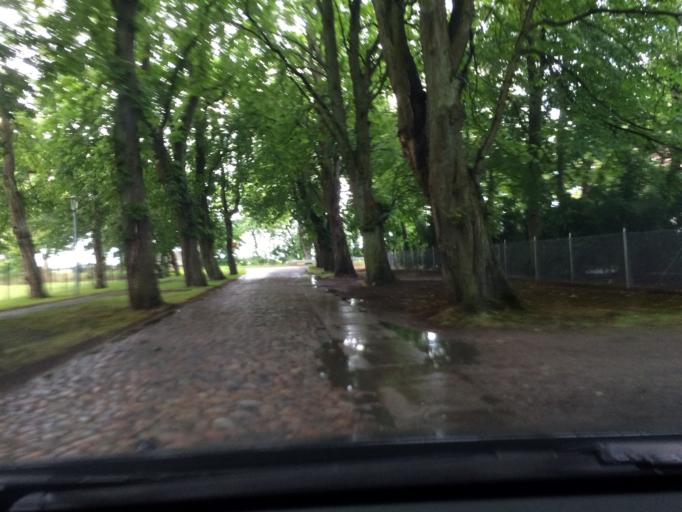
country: DE
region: Mecklenburg-Vorpommern
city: Altenpleen
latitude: 54.3976
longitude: 12.9732
